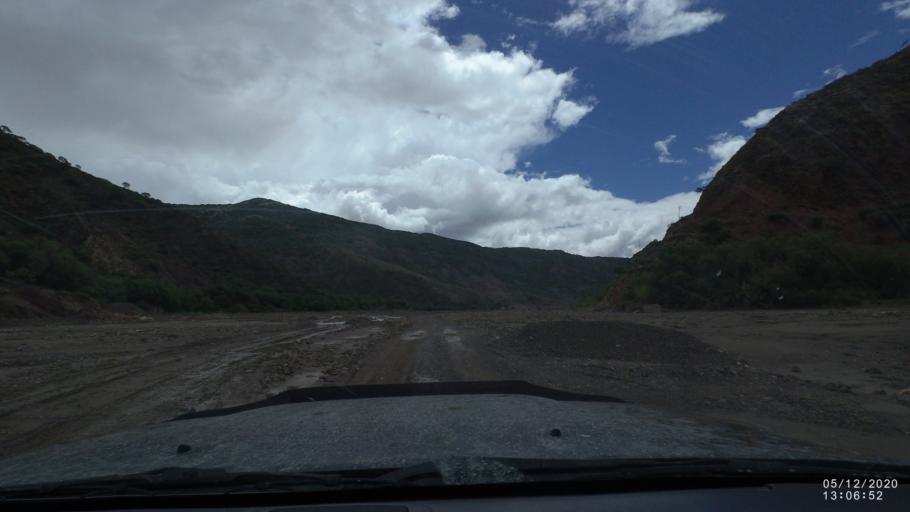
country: BO
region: Cochabamba
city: Sipe Sipe
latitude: -17.5594
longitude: -66.4462
